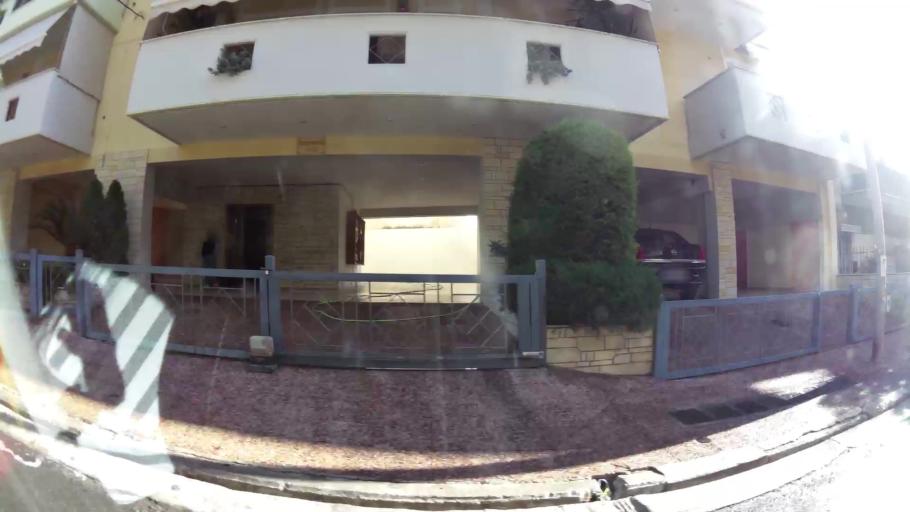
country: GR
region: Attica
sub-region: Nomos Piraios
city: Nikaia
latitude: 37.9707
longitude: 23.6579
